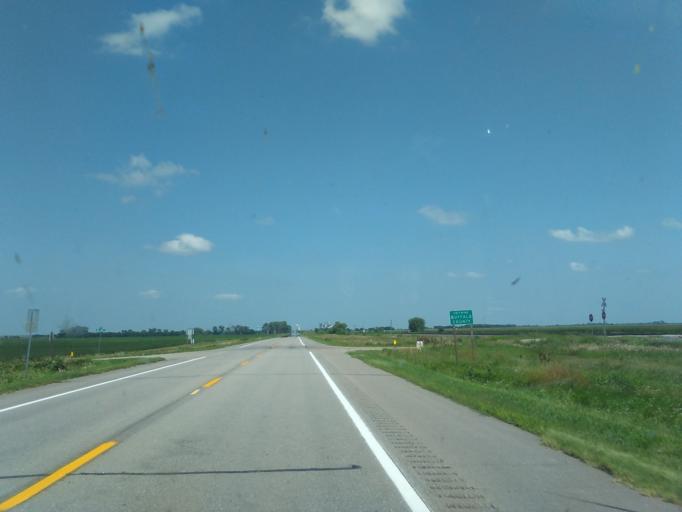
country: US
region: Nebraska
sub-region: Phelps County
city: Holdrege
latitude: 40.7243
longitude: -99.4274
